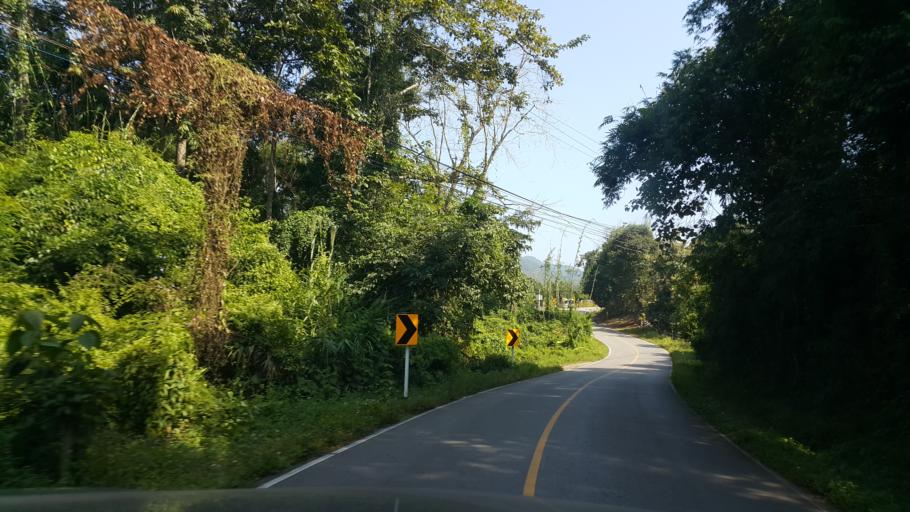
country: TH
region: Chiang Mai
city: Samoeng
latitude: 18.8658
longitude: 98.6348
